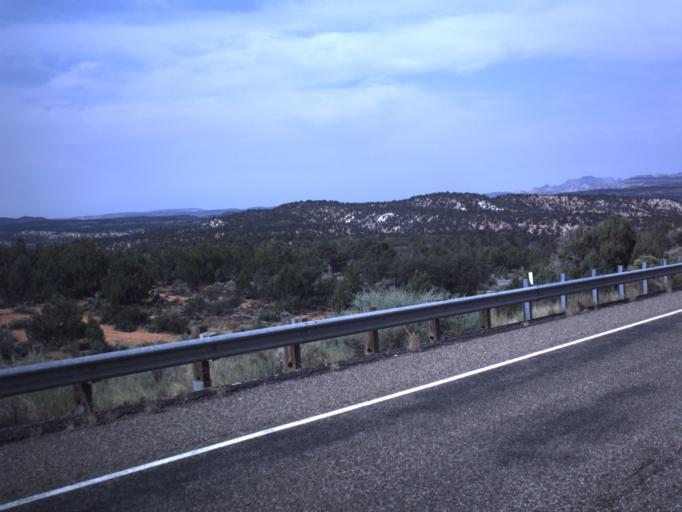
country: US
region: Utah
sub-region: Kane County
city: Kanab
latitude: 37.1862
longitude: -112.6513
